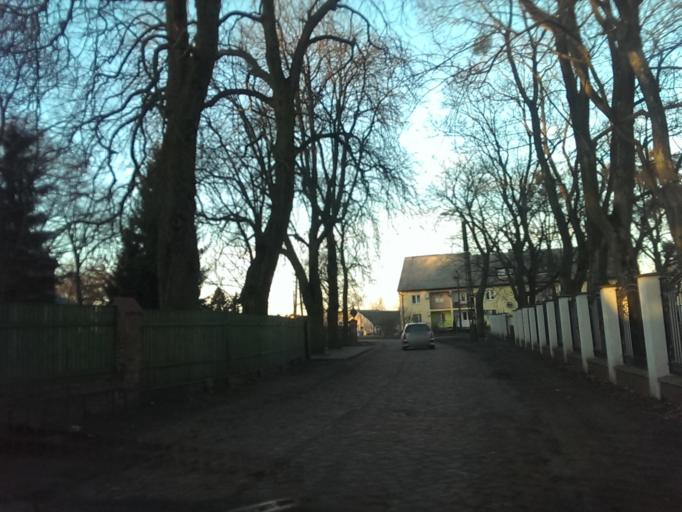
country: PL
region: Kujawsko-Pomorskie
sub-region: Powiat nakielski
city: Szubin
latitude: 53.0762
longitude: 17.6901
